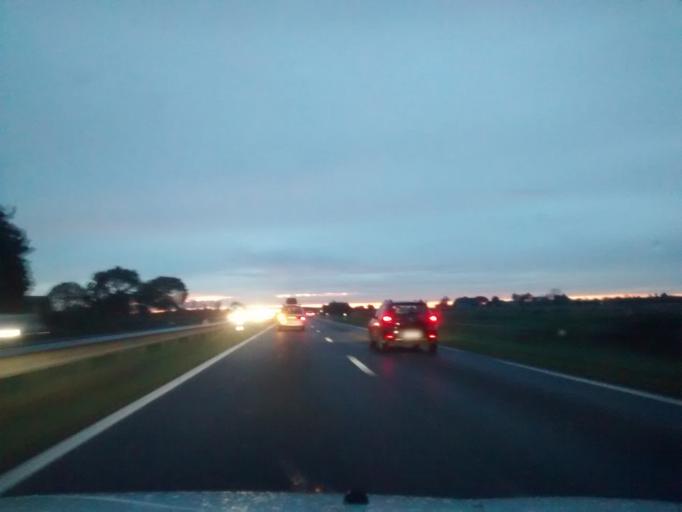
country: FR
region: Brittany
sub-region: Departement des Cotes-d'Armor
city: Pordic
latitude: 48.5450
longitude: -2.8172
